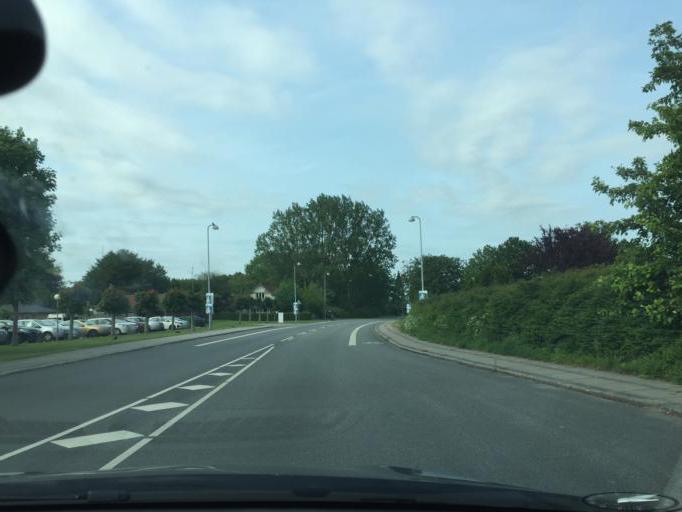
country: DK
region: South Denmark
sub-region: Odense Kommune
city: Bellinge
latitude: 55.3501
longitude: 10.3382
